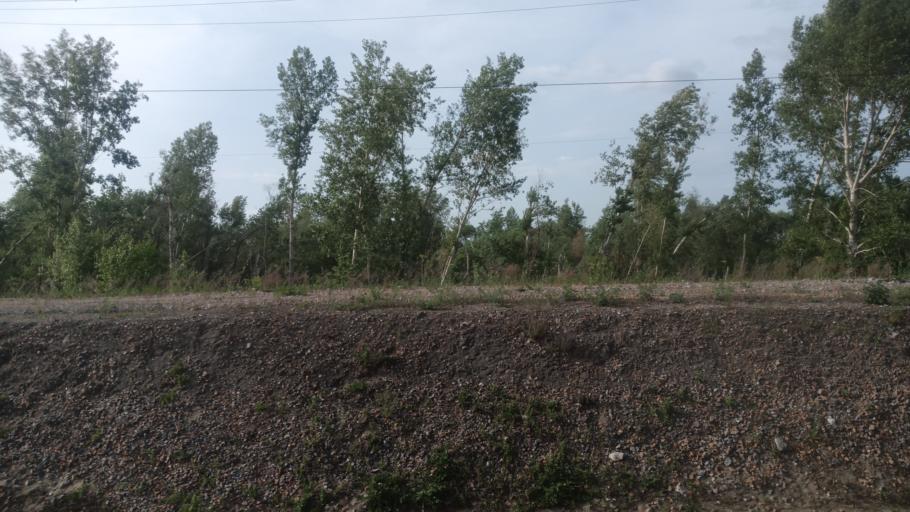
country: RU
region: Altai Krai
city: Novoaltaysk
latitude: 53.3698
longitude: 83.8606
